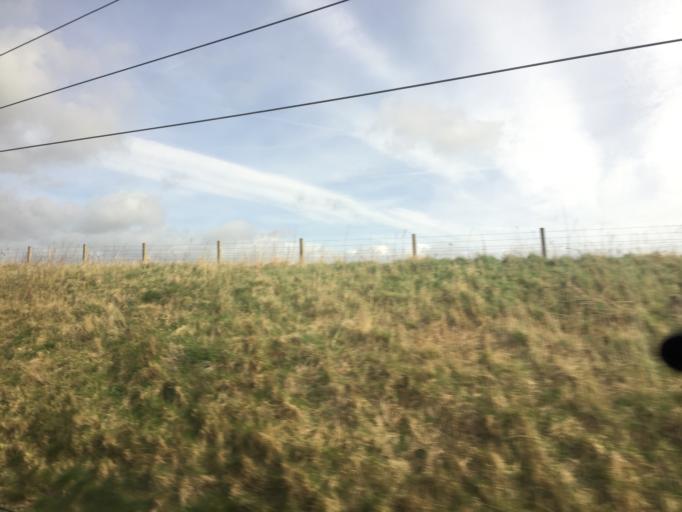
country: GB
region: England
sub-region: Cumbria
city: Penrith
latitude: 54.7313
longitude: -2.8008
